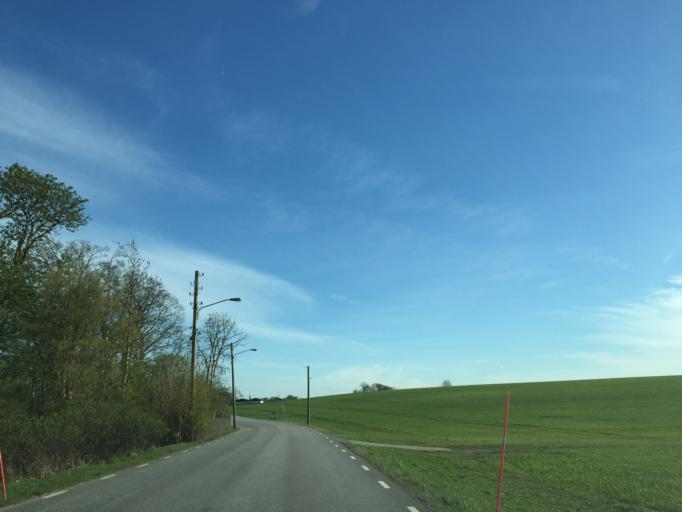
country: SE
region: Skane
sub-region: Malmo
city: Oxie
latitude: 55.5780
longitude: 13.0963
